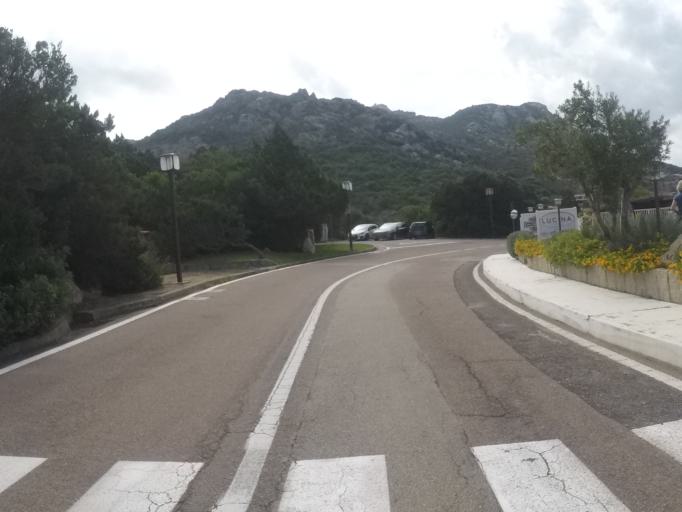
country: IT
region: Sardinia
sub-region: Provincia di Olbia-Tempio
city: Porto Cervo
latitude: 41.1325
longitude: 9.5303
